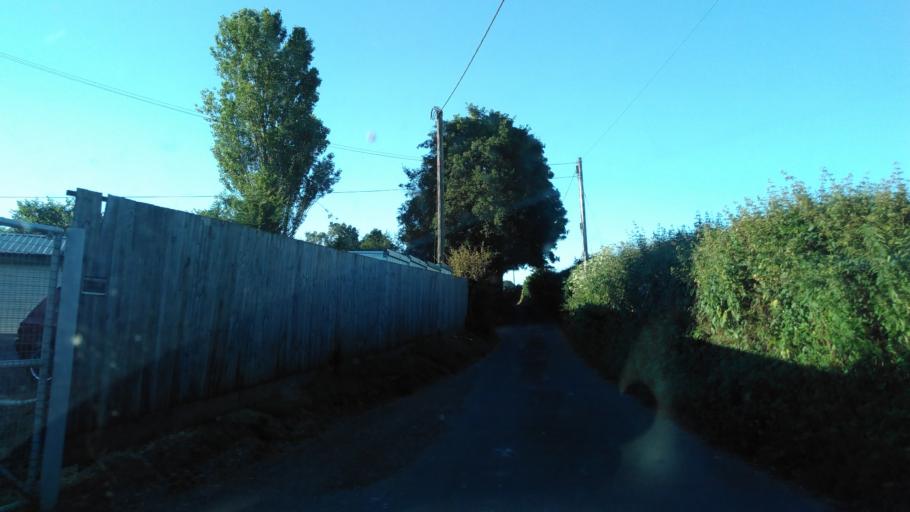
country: GB
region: England
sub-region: Kent
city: Chartham
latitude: 51.2488
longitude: 1.0027
